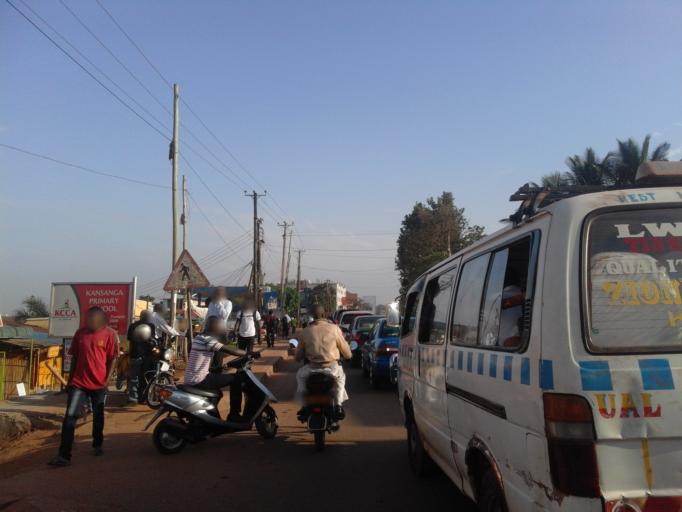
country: UG
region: Central Region
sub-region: Kampala District
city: Kampala
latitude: 0.2902
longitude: 32.6061
